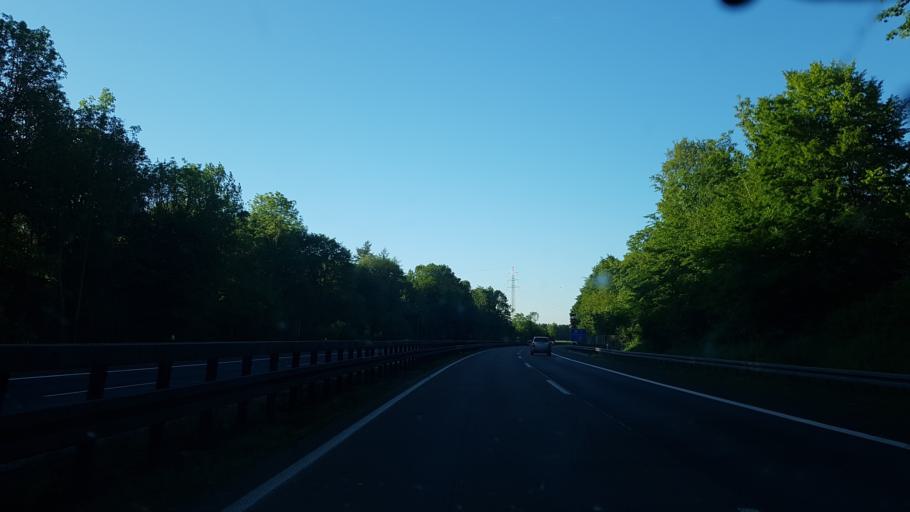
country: DE
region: North Rhine-Westphalia
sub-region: Regierungsbezirk Dusseldorf
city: Monchengladbach
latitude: 51.1632
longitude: 6.4008
